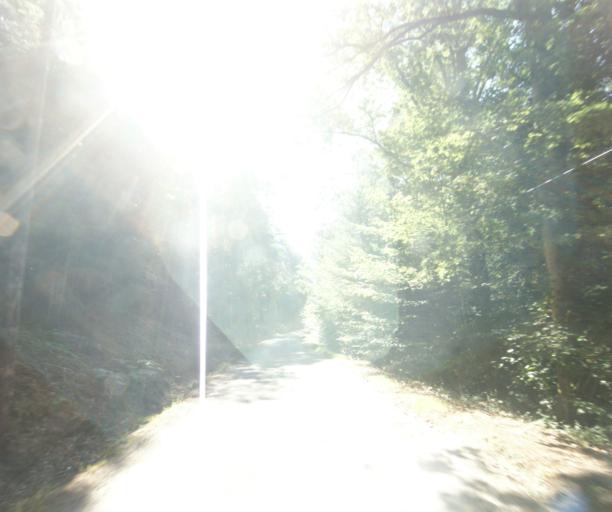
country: FR
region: Lorraine
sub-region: Departement des Vosges
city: Epinal
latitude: 48.1579
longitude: 6.4624
